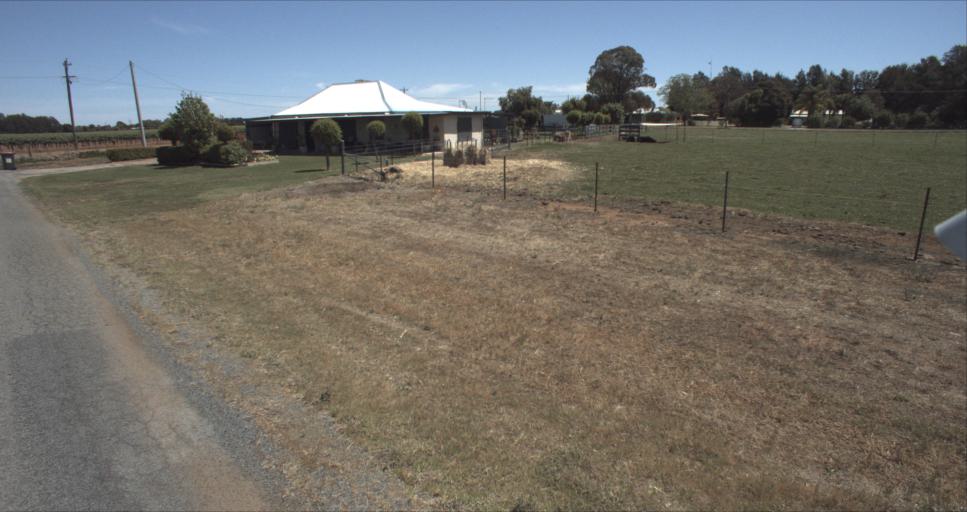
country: AU
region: New South Wales
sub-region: Leeton
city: Leeton
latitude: -34.5303
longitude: 146.3320
